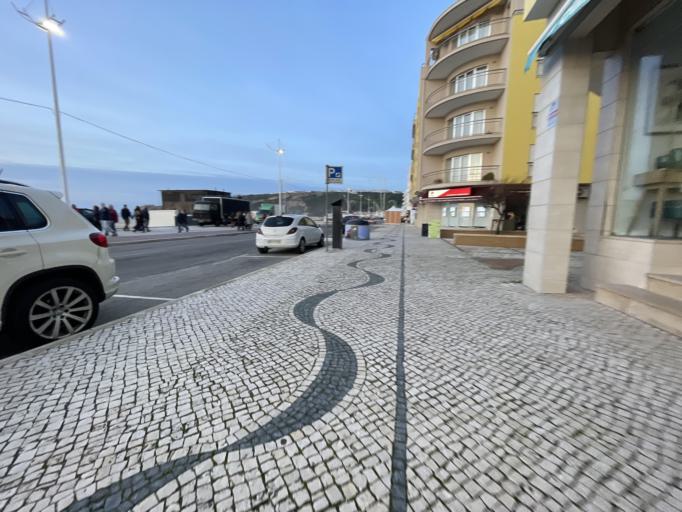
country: PT
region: Leiria
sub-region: Nazare
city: Nazare
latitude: 39.5939
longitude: -9.0724
